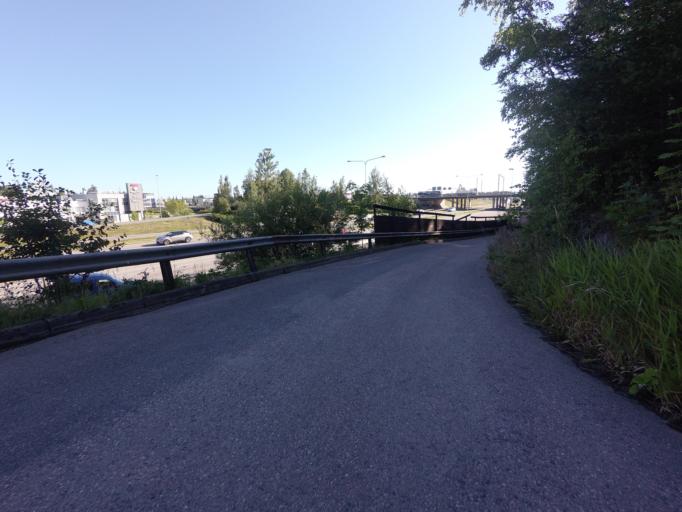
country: FI
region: Uusimaa
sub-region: Helsinki
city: Kauniainen
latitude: 60.1595
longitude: 24.7028
